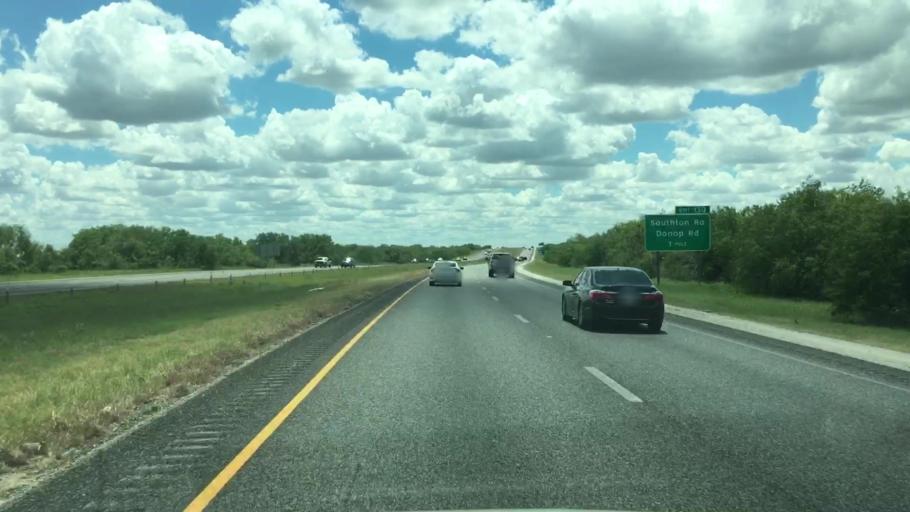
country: US
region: Texas
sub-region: Bexar County
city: Elmendorf
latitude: 29.2983
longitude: -98.3952
